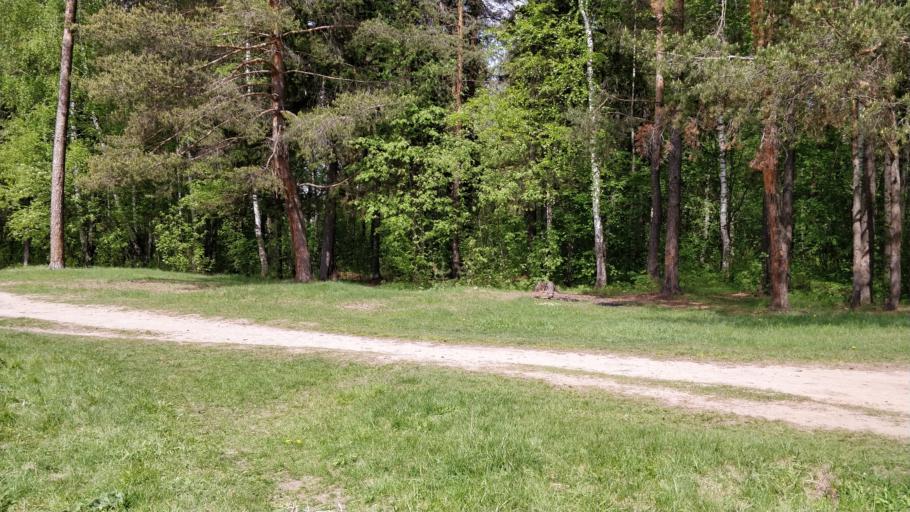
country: RU
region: Perm
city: Kondratovo
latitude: 57.9883
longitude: 56.1445
